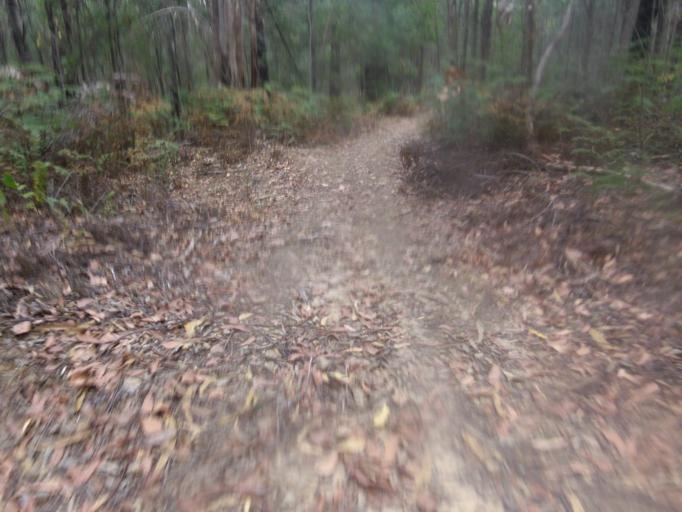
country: AU
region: Victoria
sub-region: Murrindindi
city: Alexandra
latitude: -37.3827
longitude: 145.5527
